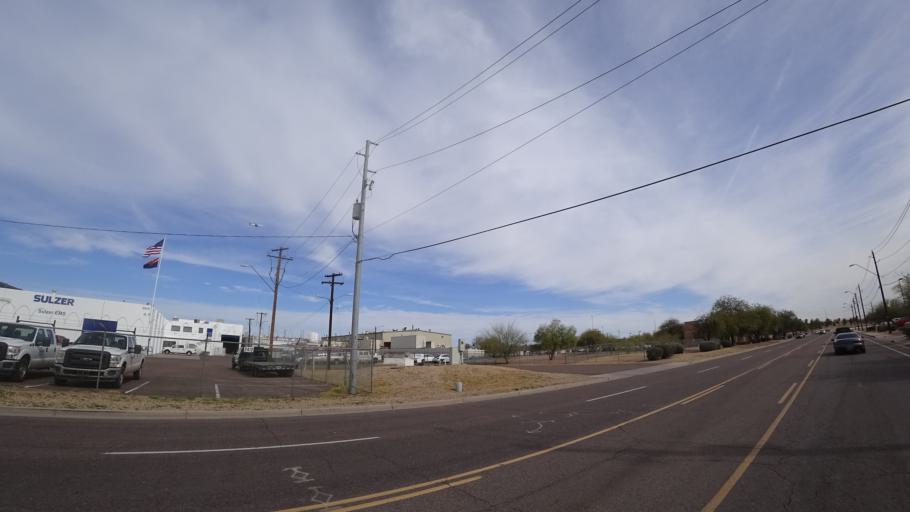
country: US
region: Arizona
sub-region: Maricopa County
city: Phoenix
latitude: 33.4295
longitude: -112.1114
